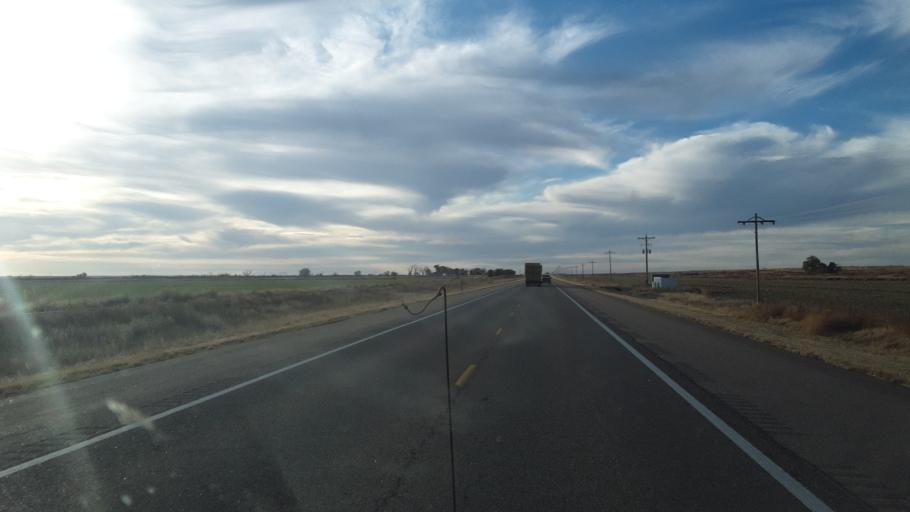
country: US
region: Kansas
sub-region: Hamilton County
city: Syracuse
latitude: 37.9450
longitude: -101.5862
